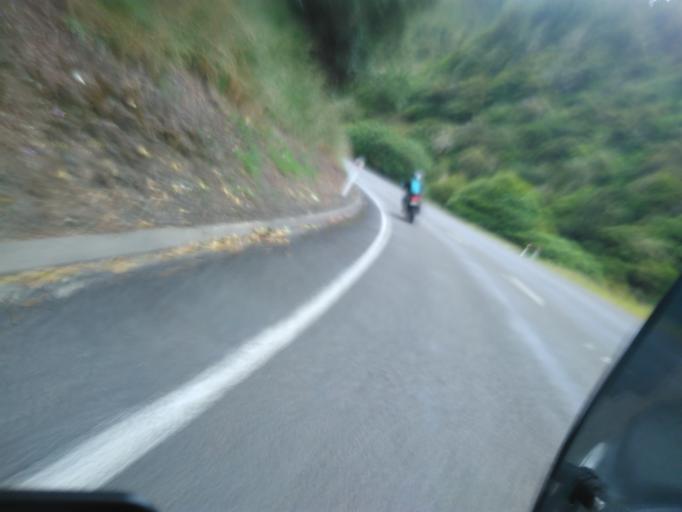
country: NZ
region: Bay of Plenty
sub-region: Opotiki District
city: Opotiki
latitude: -38.3088
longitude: 177.3933
